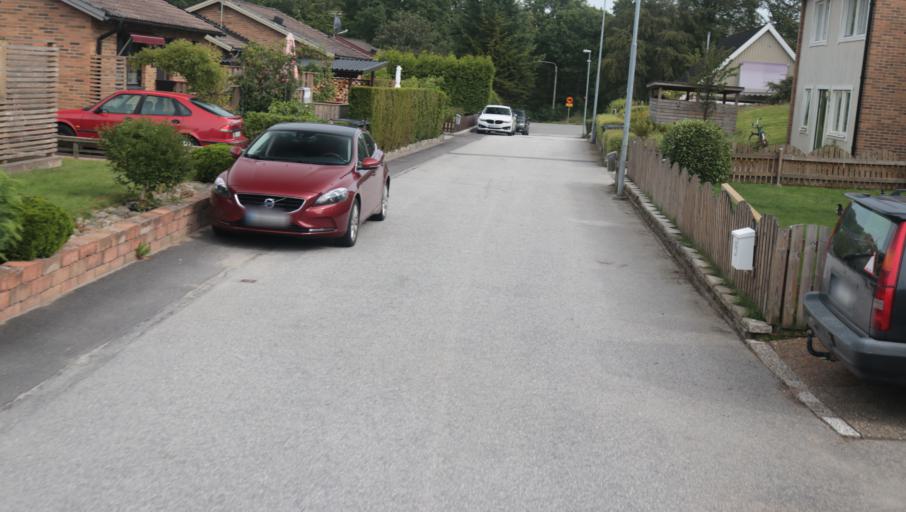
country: SE
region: Blekinge
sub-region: Karlshamns Kommun
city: Karlshamn
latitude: 56.2044
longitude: 14.8597
